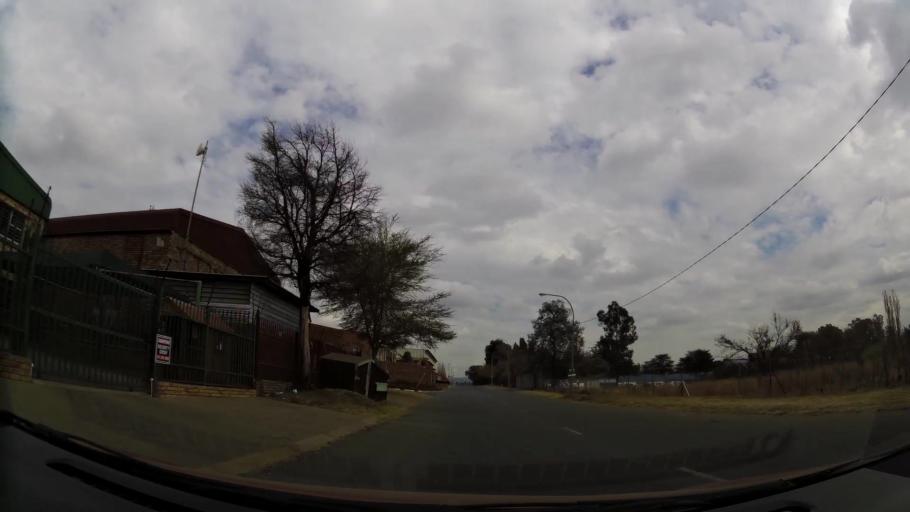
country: ZA
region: Gauteng
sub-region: West Rand District Municipality
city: Muldersdriseloop
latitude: -26.0785
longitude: 27.9111
